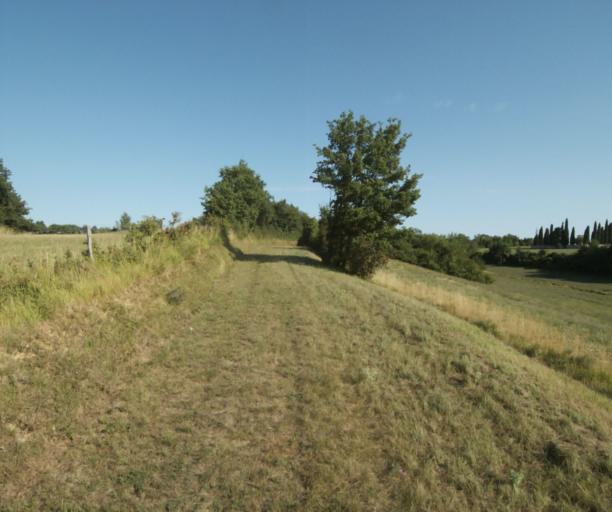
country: FR
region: Midi-Pyrenees
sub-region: Departement de la Haute-Garonne
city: Saint-Felix-Lauragais
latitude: 43.4454
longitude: 1.8198
